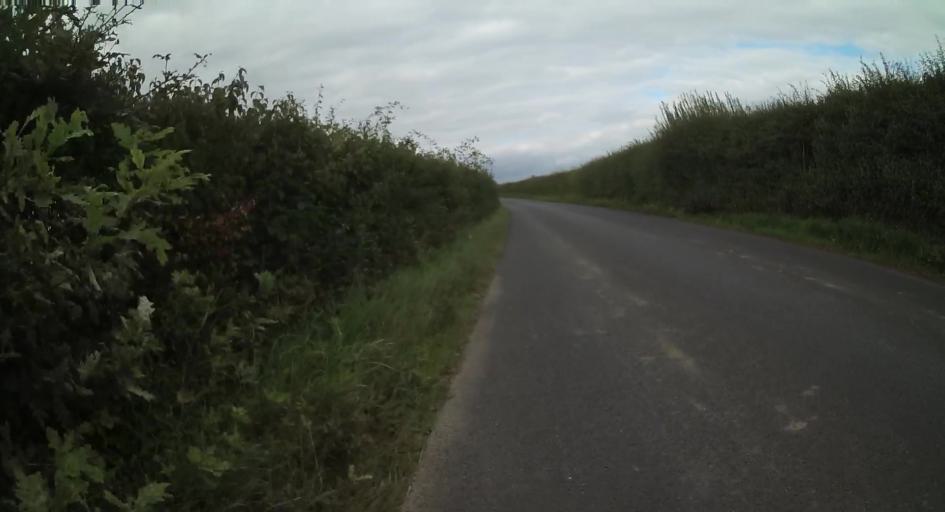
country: GB
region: England
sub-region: Isle of Wight
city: Yarmouth
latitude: 50.6942
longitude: -1.4838
